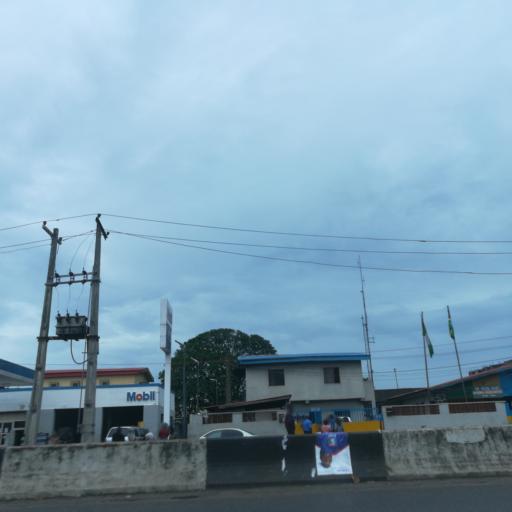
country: NG
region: Lagos
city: Makoko
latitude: 6.5056
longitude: 3.3779
